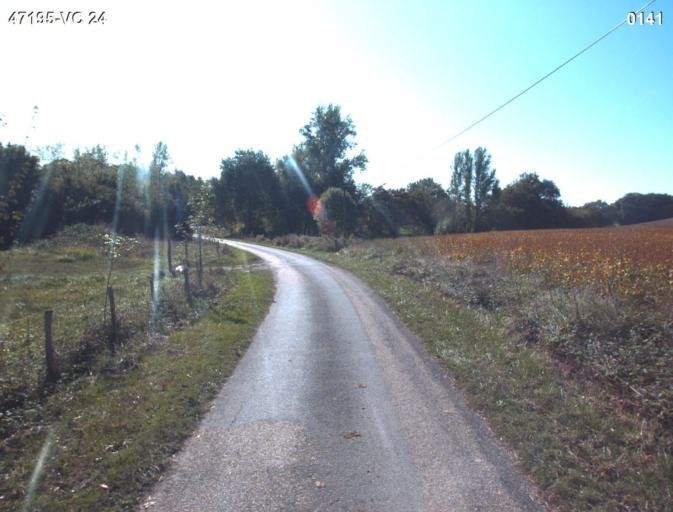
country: FR
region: Aquitaine
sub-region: Departement du Lot-et-Garonne
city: Nerac
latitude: 44.1630
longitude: 0.3647
